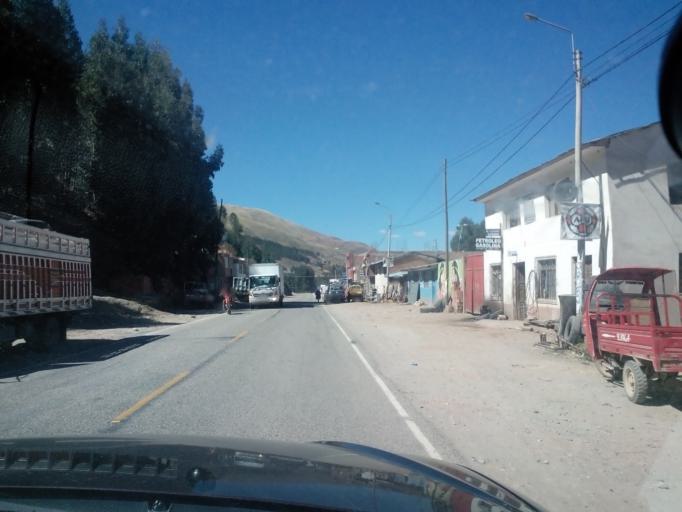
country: PE
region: Cusco
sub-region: Provincia de Canchis
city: Combapata
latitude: -14.1014
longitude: -71.4279
